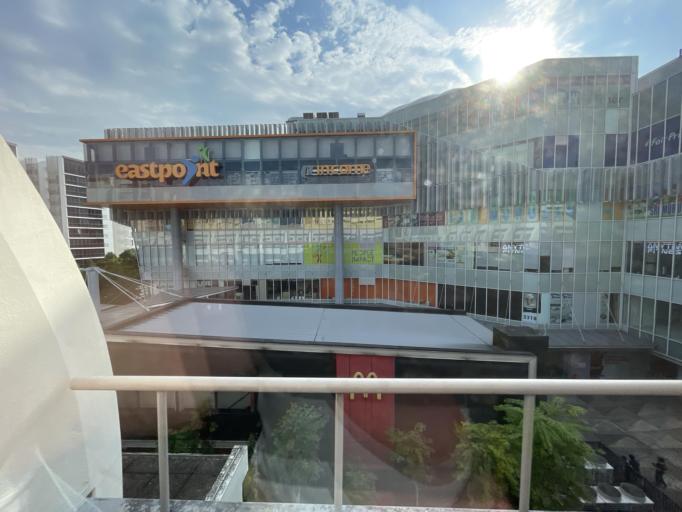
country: SG
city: Singapore
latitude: 1.3429
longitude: 103.9536
